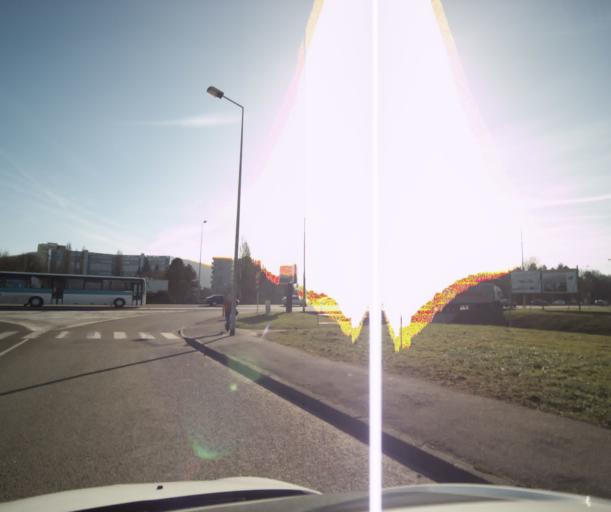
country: FR
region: Franche-Comte
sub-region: Departement du Doubs
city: Avanne-Aveney
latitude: 47.2255
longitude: 5.9725
